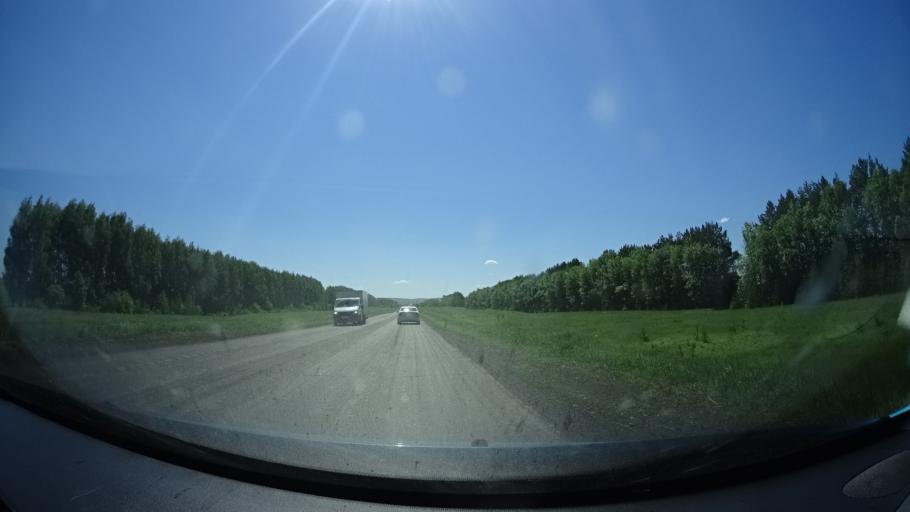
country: RU
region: Bashkortostan
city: Blagoveshchensk
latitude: 55.2335
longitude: 55.7795
